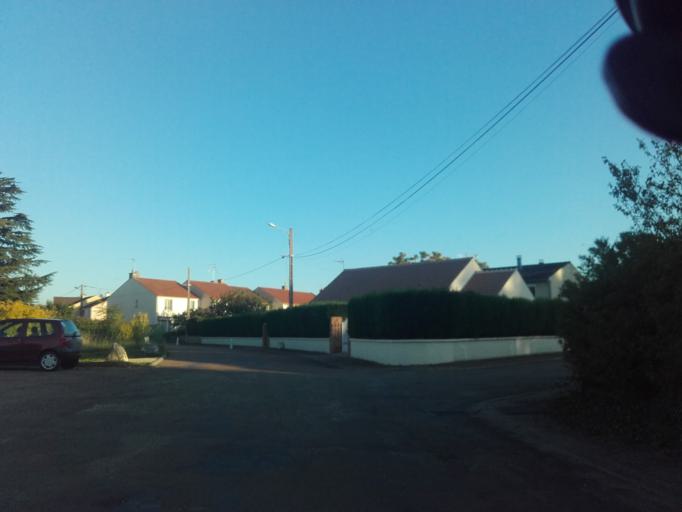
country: FR
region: Bourgogne
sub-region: Departement de Saone-et-Loire
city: Chagny
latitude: 46.8996
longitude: 4.7558
